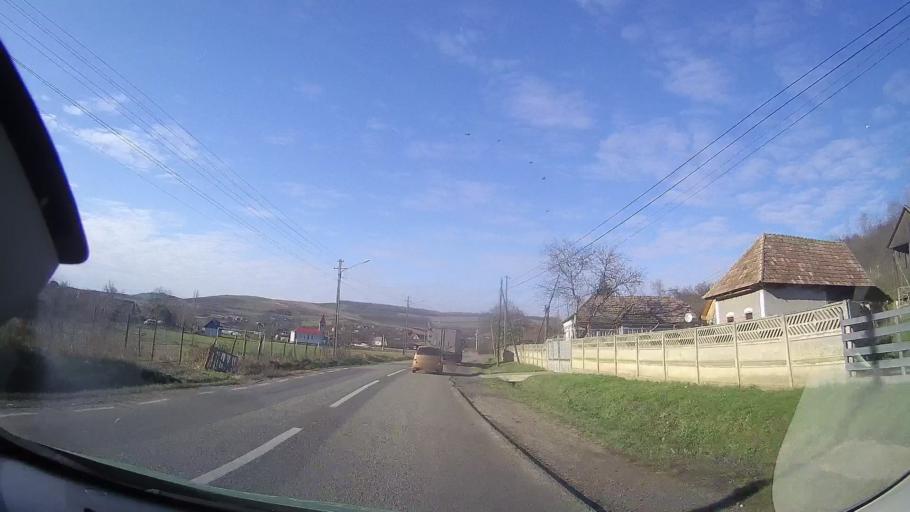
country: RO
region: Cluj
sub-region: Comuna Caianu
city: Vaida-Camaras
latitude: 46.8062
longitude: 23.9745
